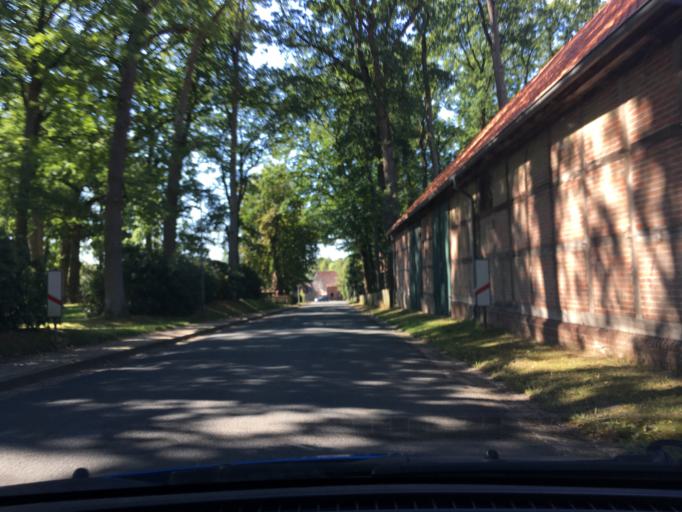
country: DE
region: Lower Saxony
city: Bergen
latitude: 52.8301
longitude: 9.9361
